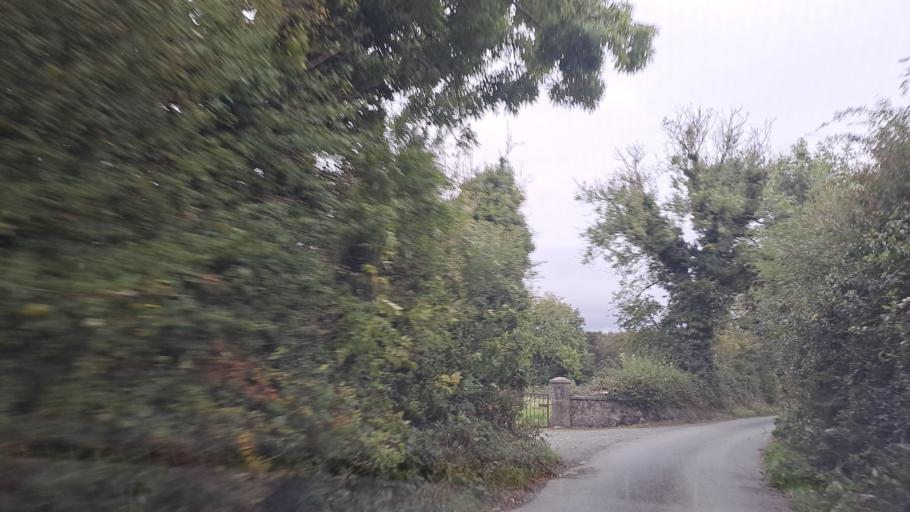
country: IE
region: Ulster
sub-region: An Cabhan
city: Bailieborough
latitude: 53.9855
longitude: -6.8853
